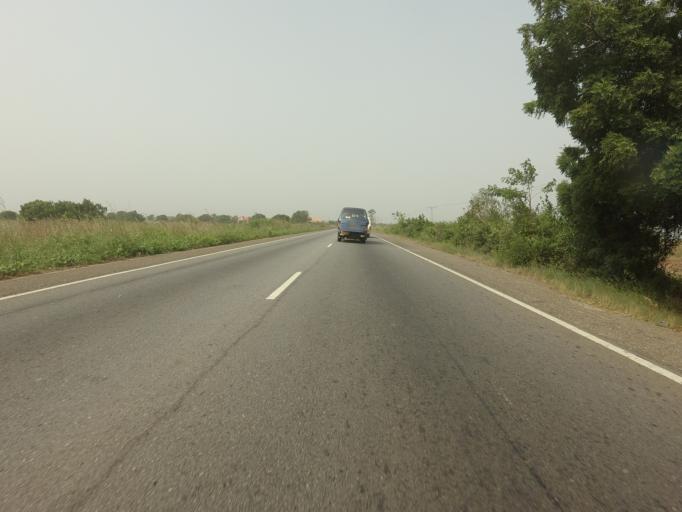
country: GH
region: Volta
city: Anloga
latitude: 5.9237
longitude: 0.5231
